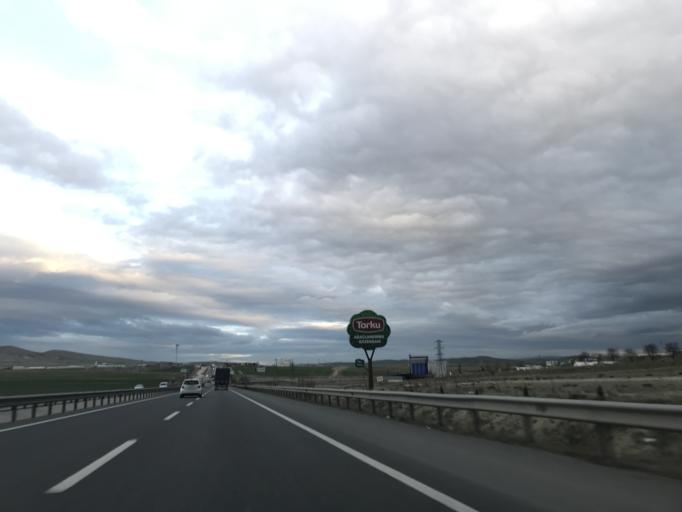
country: TR
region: Ankara
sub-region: Goelbasi
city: Golbasi
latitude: 39.6468
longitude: 32.8201
